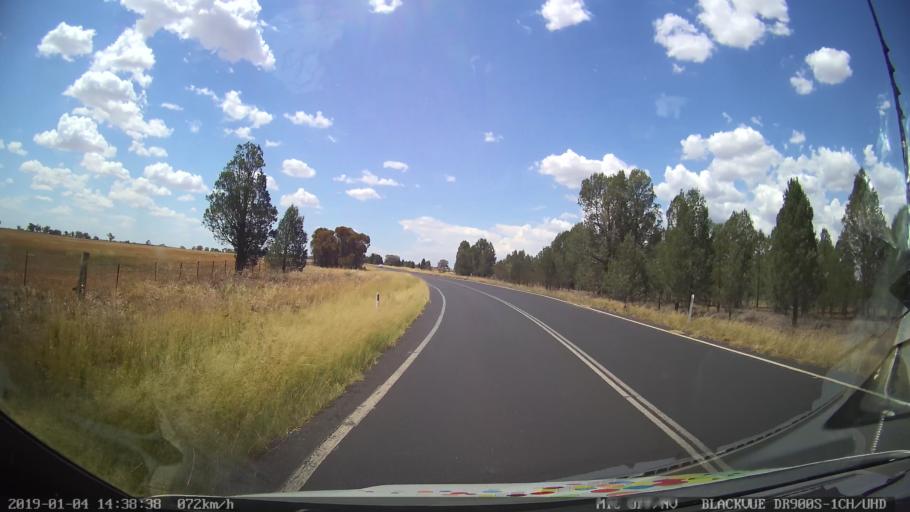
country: AU
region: New South Wales
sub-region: Dubbo Municipality
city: Dubbo
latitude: -32.1741
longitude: 148.6311
